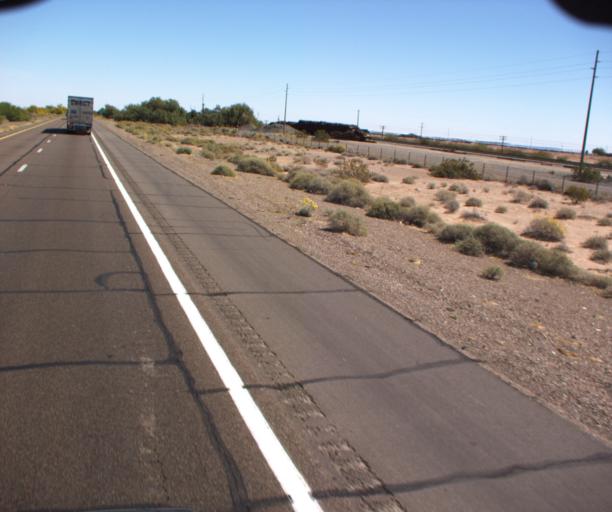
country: US
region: Arizona
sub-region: Yuma County
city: Wellton
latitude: 32.8232
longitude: -113.4526
